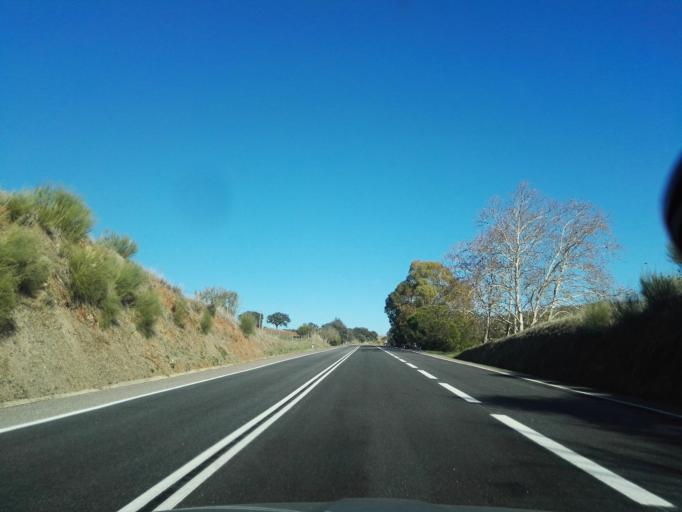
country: PT
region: Evora
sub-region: Vila Vicosa
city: Vila Vicosa
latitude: 38.8433
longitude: -7.3837
